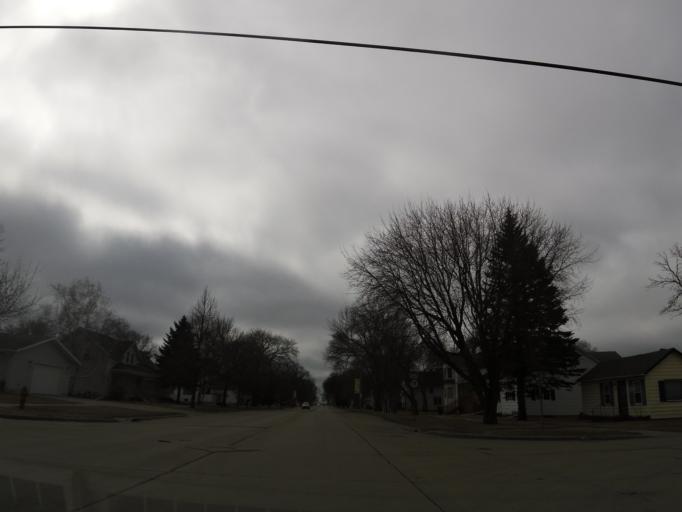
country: US
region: North Dakota
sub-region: Cass County
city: Casselton
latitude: 46.8988
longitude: -97.2115
